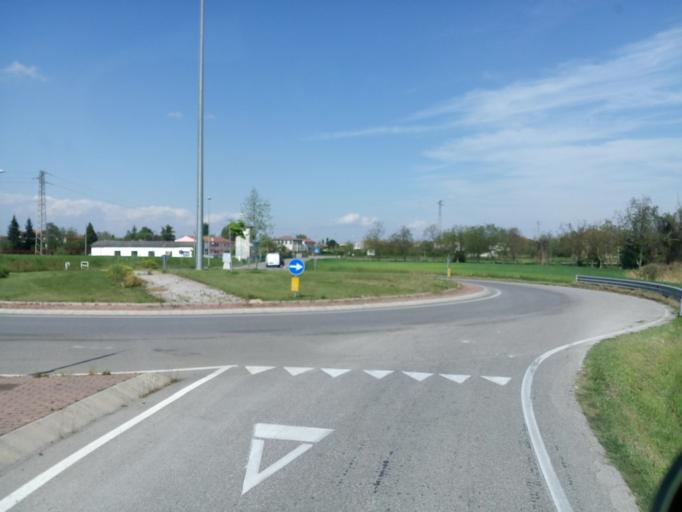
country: IT
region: Veneto
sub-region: Provincia di Verona
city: Cerea
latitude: 45.1965
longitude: 11.1950
